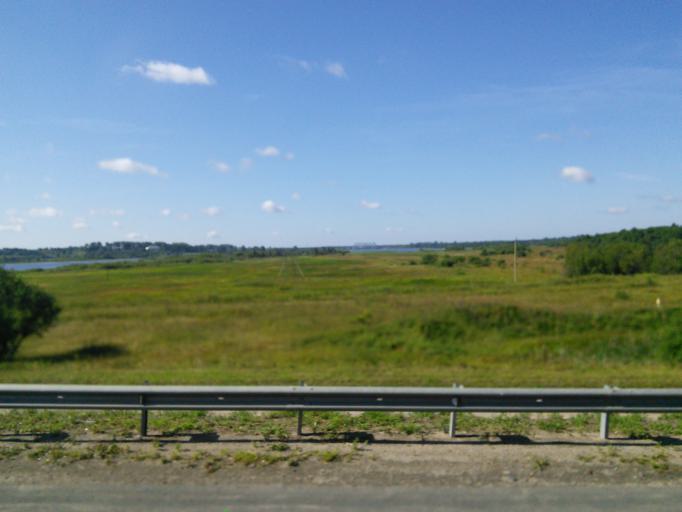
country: RU
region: Vologda
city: Sheksna
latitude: 59.2163
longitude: 38.4891
